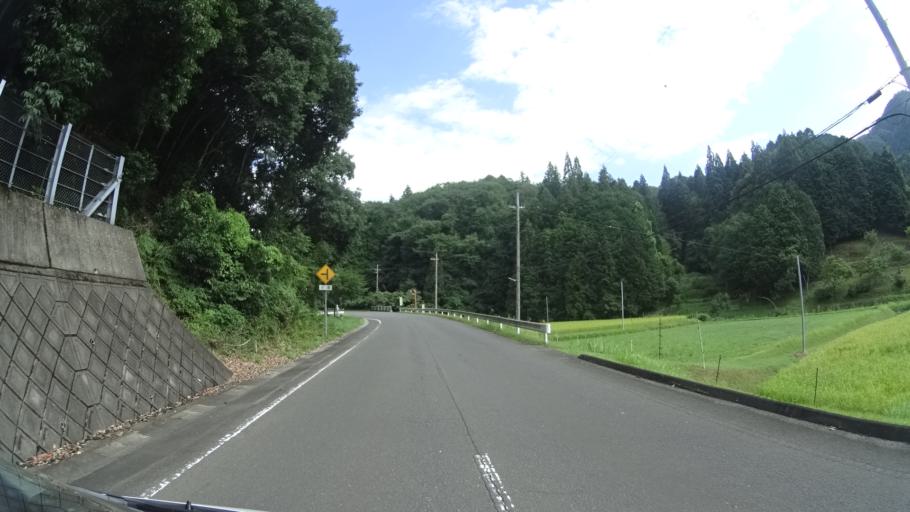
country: JP
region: Kyoto
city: Fukuchiyama
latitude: 35.3585
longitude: 135.1405
